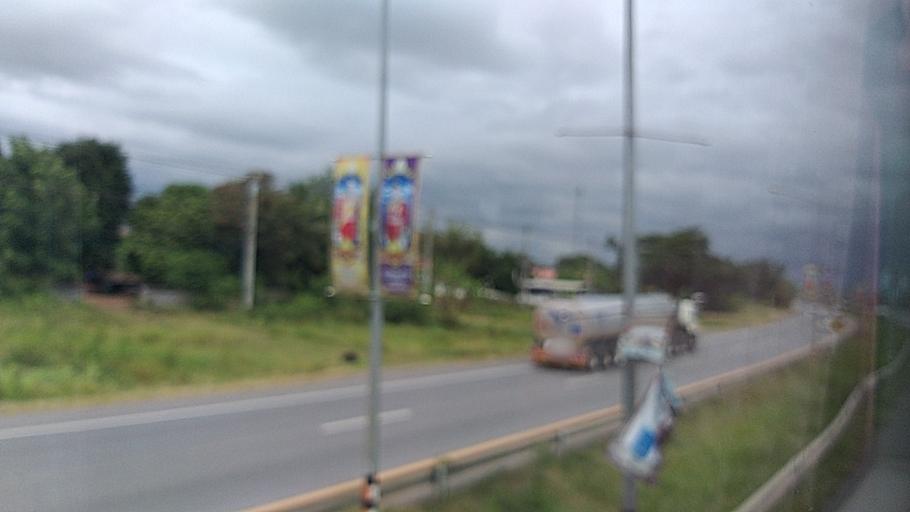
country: TH
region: Khon Kaen
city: Non Sila
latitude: 15.9606
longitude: 102.6895
